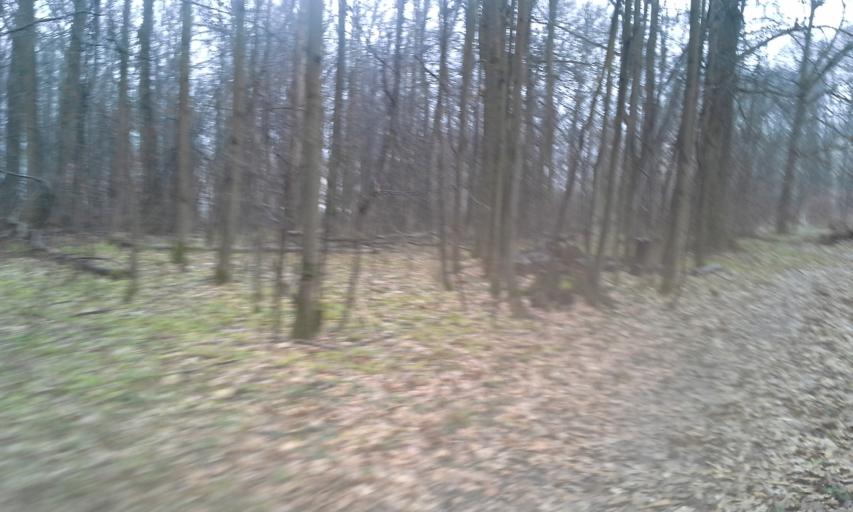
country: RU
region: Moskovskaya
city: Kommunarka
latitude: 55.5776
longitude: 37.4932
